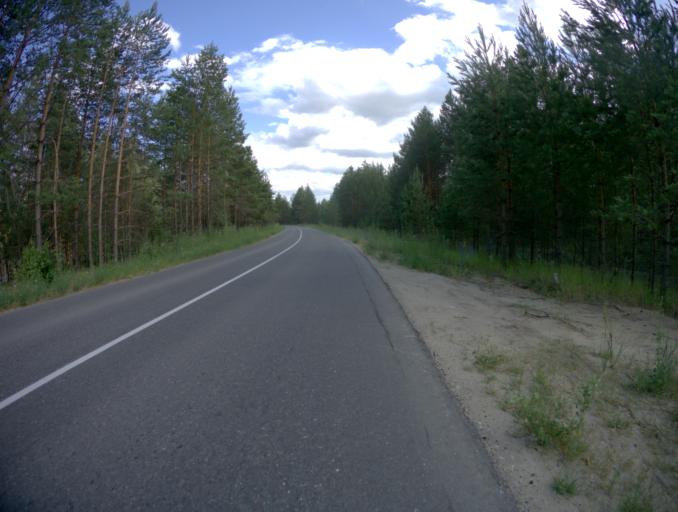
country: RU
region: Nizjnij Novgorod
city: Frolishchi
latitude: 56.3511
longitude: 42.7359
